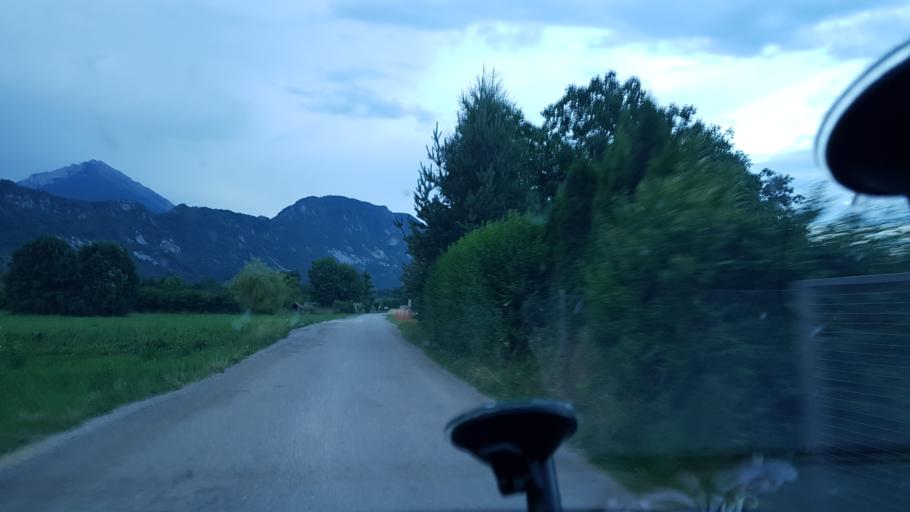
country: SI
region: Zirovnica
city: Zirovnica
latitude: 46.3934
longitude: 14.1308
